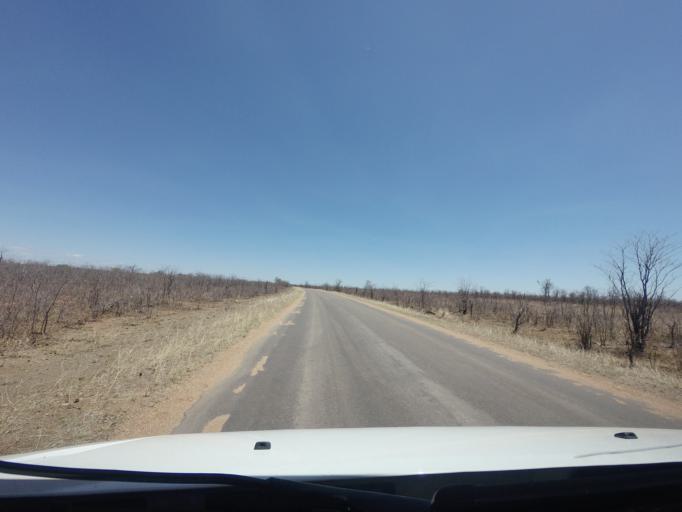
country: ZA
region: Limpopo
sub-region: Mopani District Municipality
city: Phalaborwa
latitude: -23.5530
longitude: 31.4412
